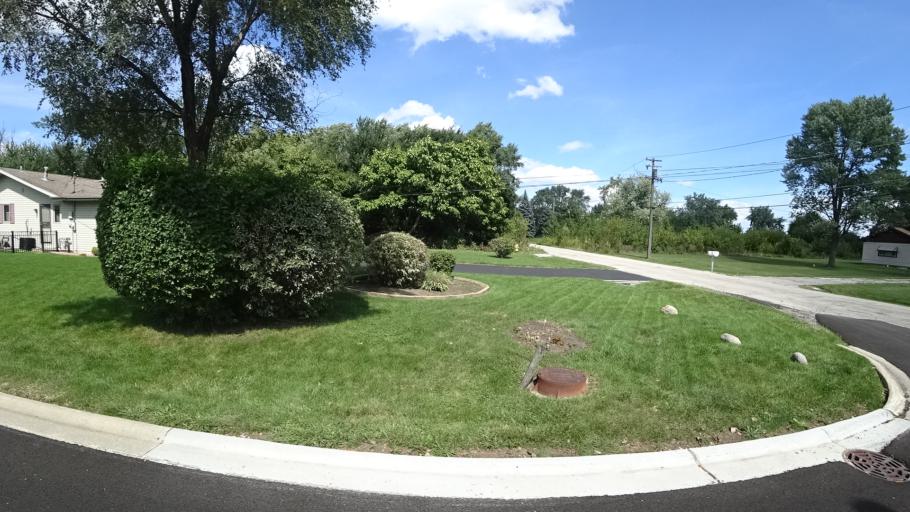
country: US
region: Illinois
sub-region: Cook County
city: Tinley Park
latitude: 41.5608
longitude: -87.7885
